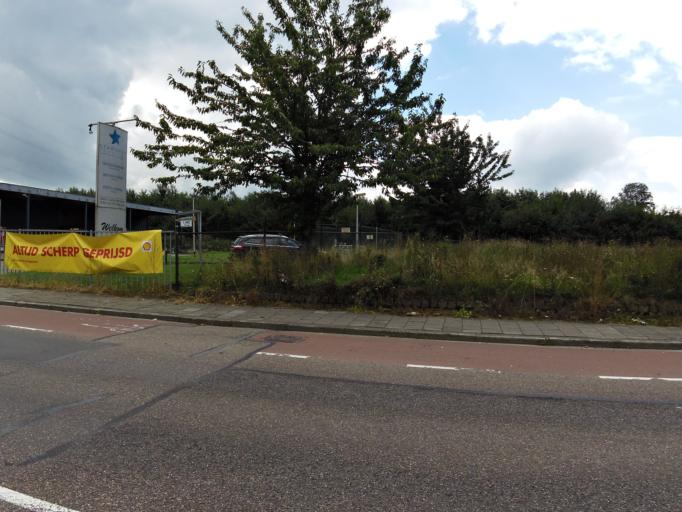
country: NL
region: Limburg
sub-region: Gemeente Heerlen
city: Heerlen
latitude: 50.8621
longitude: 6.0058
